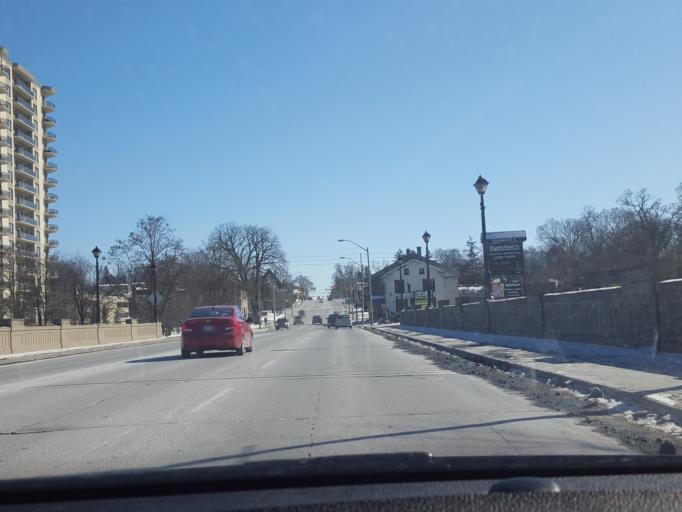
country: CA
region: Ontario
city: Cambridge
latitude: 43.3999
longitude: -80.3661
